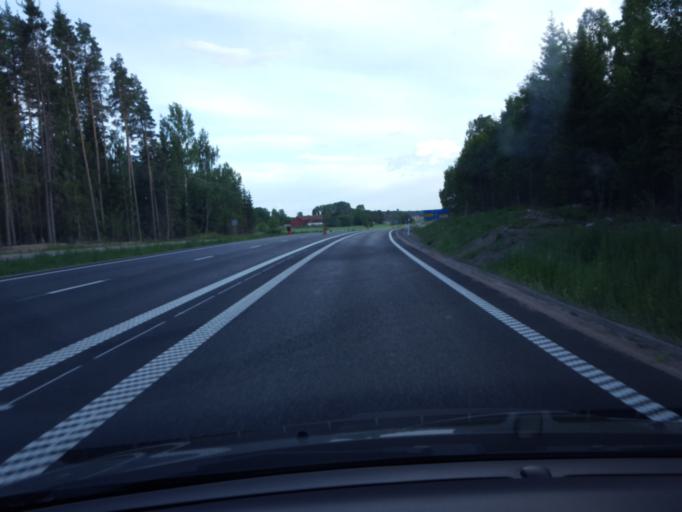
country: SE
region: Uppsala
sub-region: Osthammars Kommun
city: Gimo
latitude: 60.0981
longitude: 18.1254
